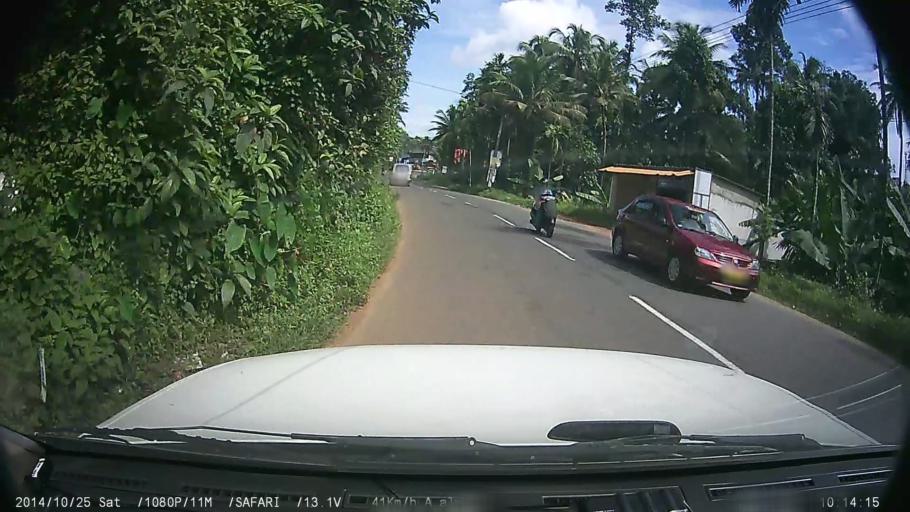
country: IN
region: Kerala
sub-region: Ernakulam
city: Piravam
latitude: 9.8666
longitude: 76.5969
